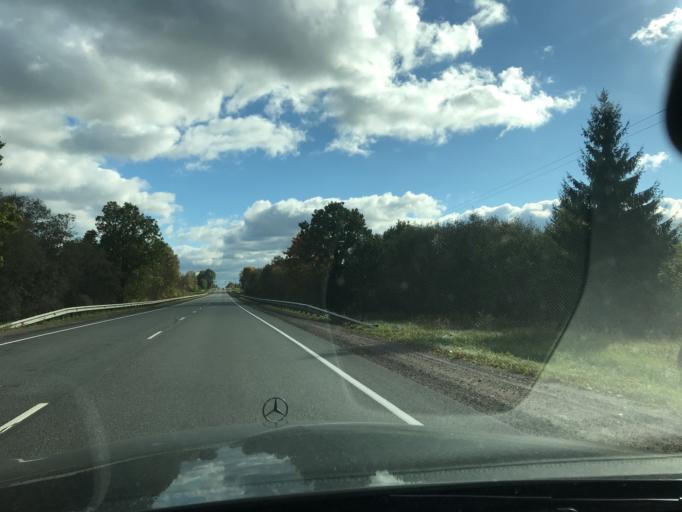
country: RU
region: Pskov
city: Ostrov
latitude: 57.1364
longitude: 28.5147
